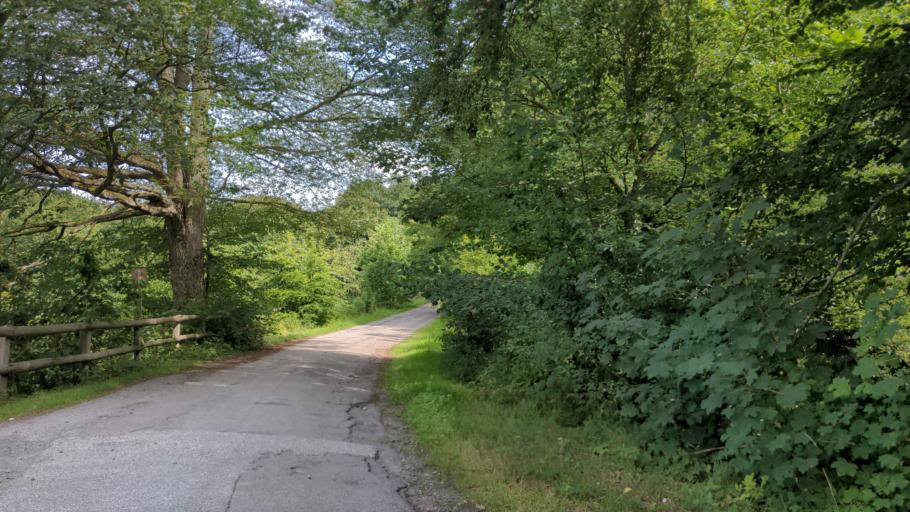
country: DE
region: Schleswig-Holstein
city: Eutin
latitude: 54.1808
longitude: 10.6342
